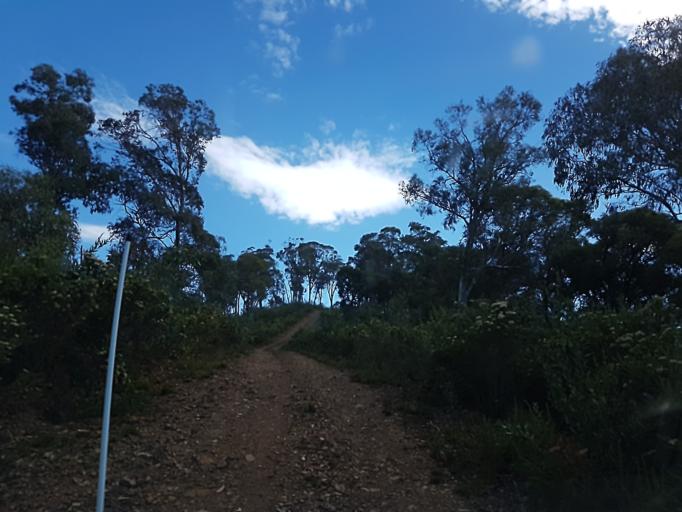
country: AU
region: Victoria
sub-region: Alpine
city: Mount Beauty
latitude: -36.9119
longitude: 147.0124
